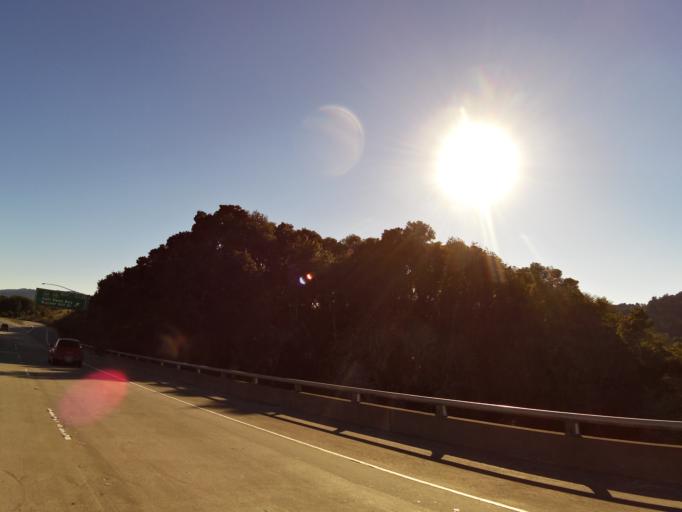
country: US
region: California
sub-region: San Mateo County
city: Highlands-Baywood Park
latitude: 37.5289
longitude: -122.3601
